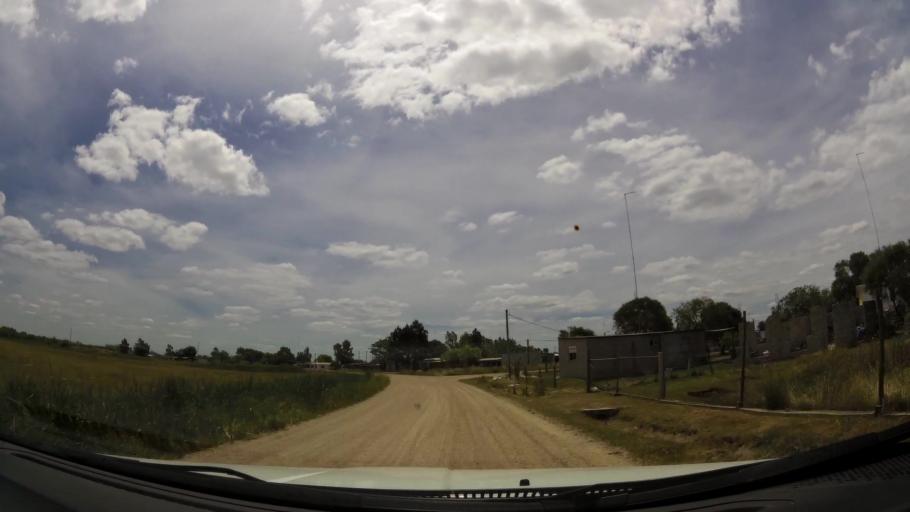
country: UY
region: San Jose
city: Delta del Tigre
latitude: -34.7609
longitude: -56.4114
